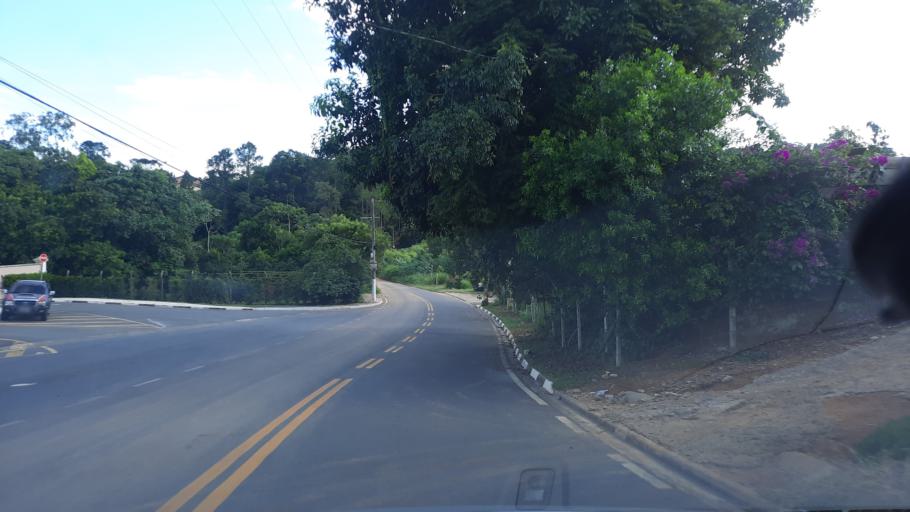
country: BR
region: Sao Paulo
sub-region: Atibaia
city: Atibaia
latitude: -23.0815
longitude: -46.5096
